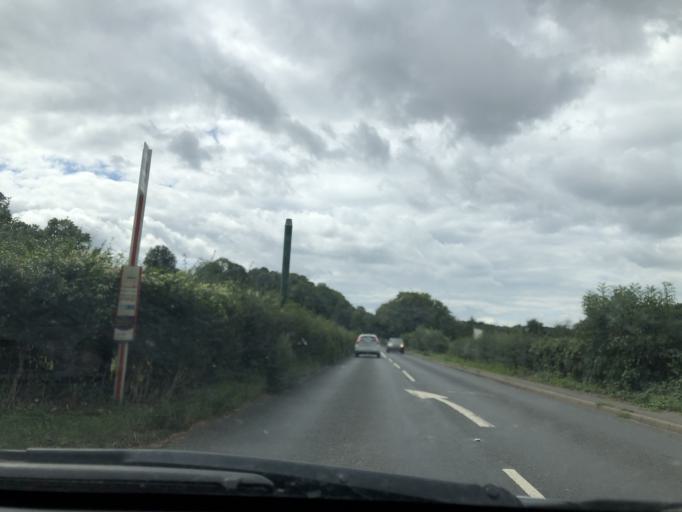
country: GB
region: England
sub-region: Kent
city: Westerham
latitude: 51.2694
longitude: 0.0834
